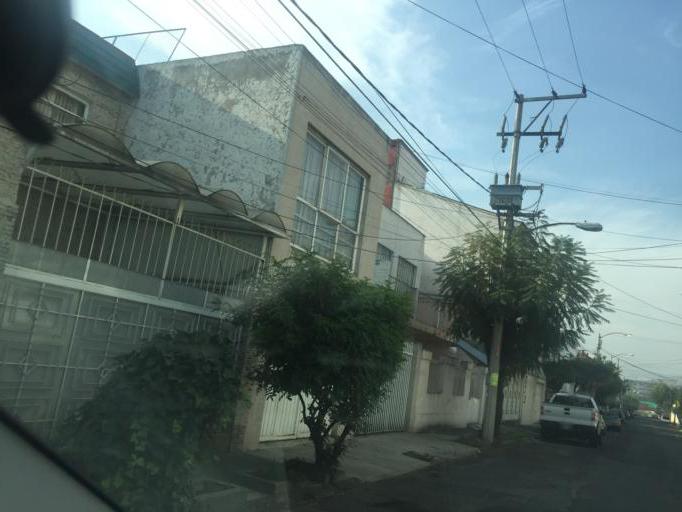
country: MX
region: Mexico
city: Colonia Lindavista
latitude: 19.4903
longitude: -99.1347
